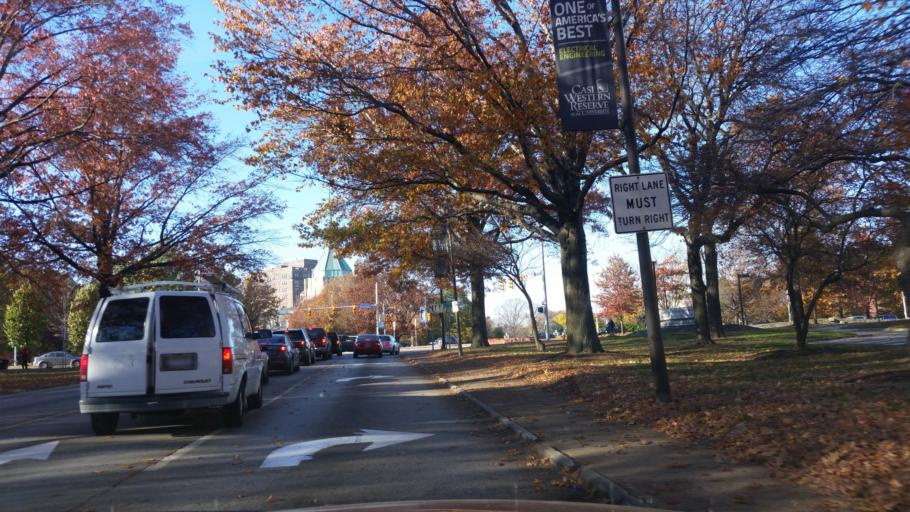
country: US
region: Ohio
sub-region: Cuyahoga County
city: Bratenahl
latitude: 41.5040
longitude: -81.6102
